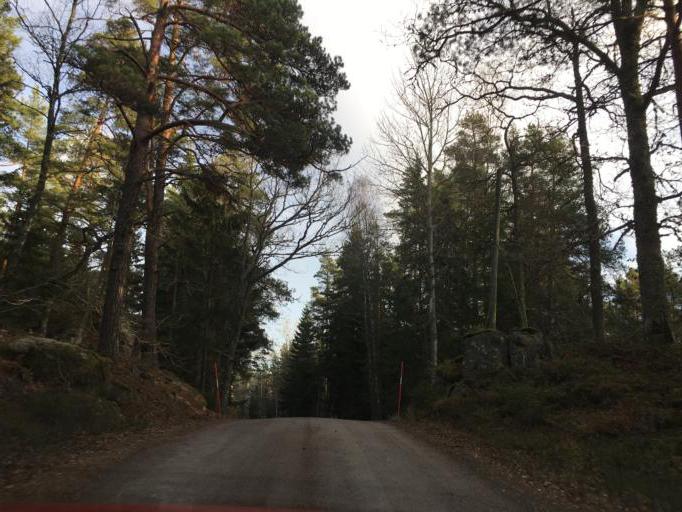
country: SE
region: Kalmar
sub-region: Vasterviks Kommun
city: Vaestervik
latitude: 57.6211
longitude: 16.5453
